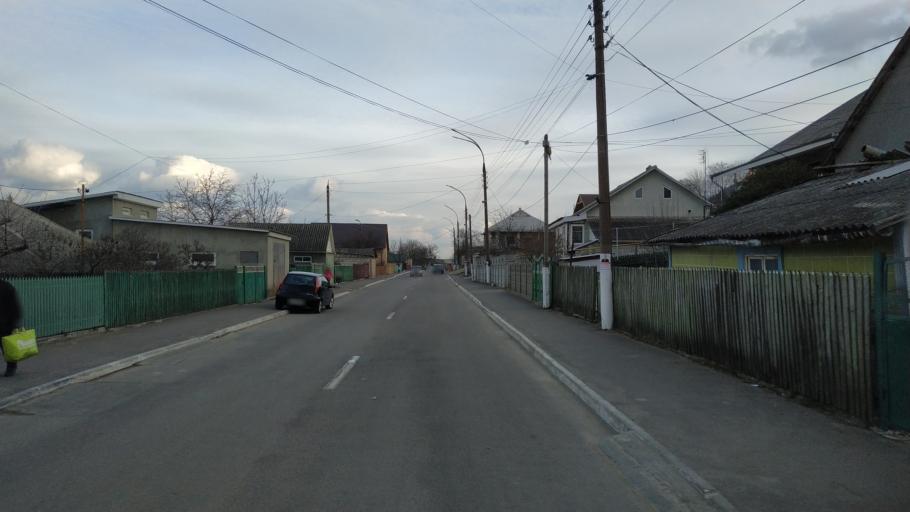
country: MD
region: Hincesti
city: Hincesti
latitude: 46.8279
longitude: 28.5934
